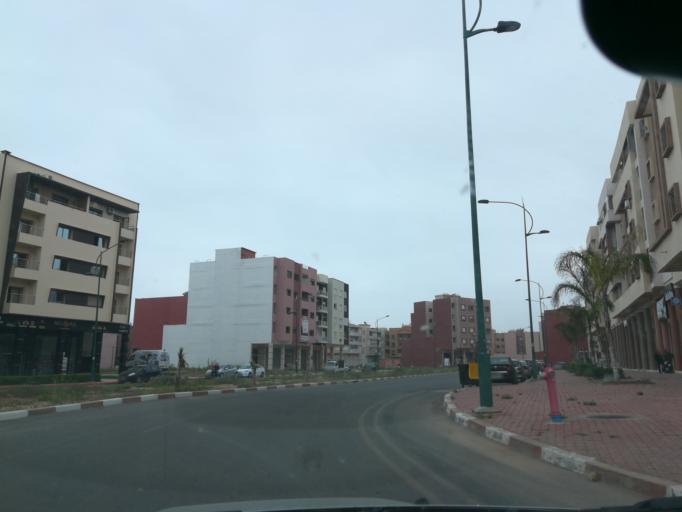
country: MA
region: Marrakech-Tensift-Al Haouz
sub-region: Marrakech
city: Marrakesh
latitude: 31.6749
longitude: -8.0244
